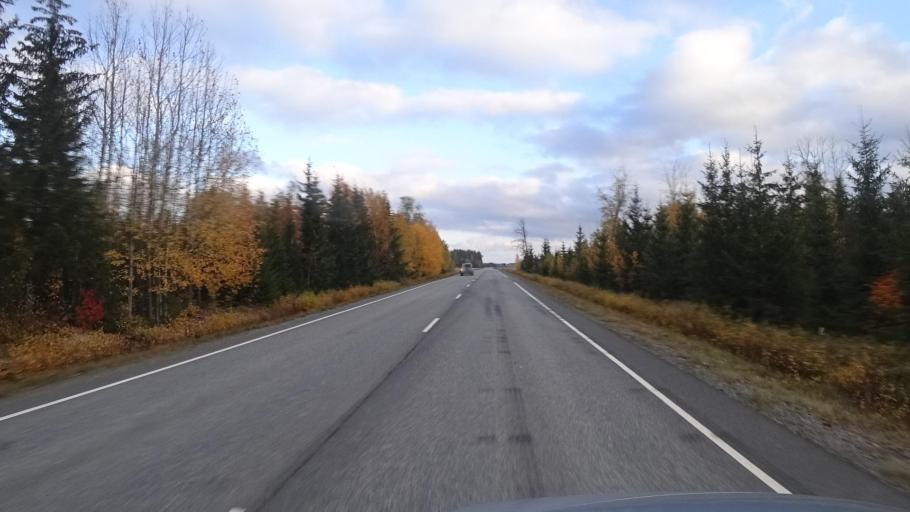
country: FI
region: Varsinais-Suomi
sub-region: Loimaa
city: Alastaro
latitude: 60.9034
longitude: 22.9356
